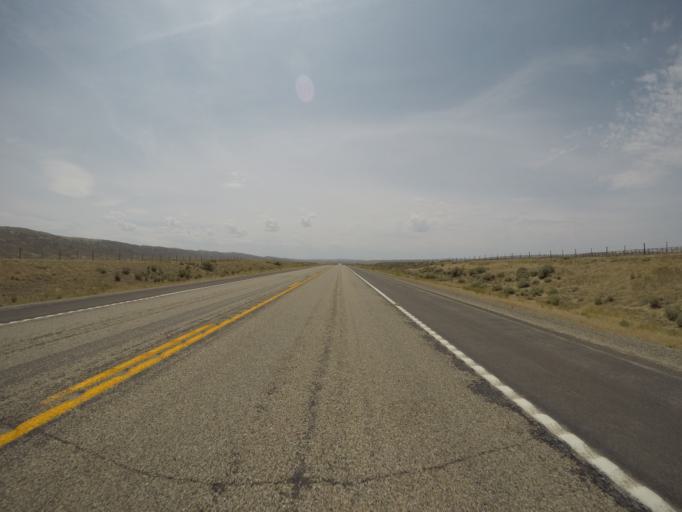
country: US
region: Wyoming
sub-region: Lincoln County
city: Kemmerer
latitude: 41.6743
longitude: -110.5688
